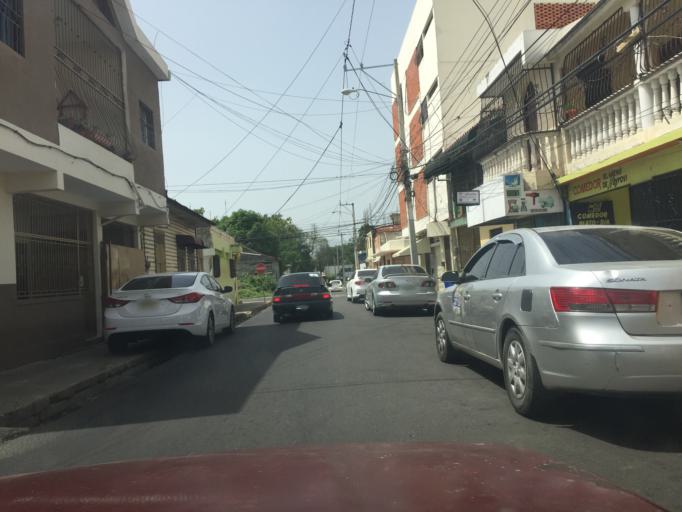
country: DO
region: Santiago
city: Santiago de los Caballeros
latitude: 19.4547
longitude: -70.7086
